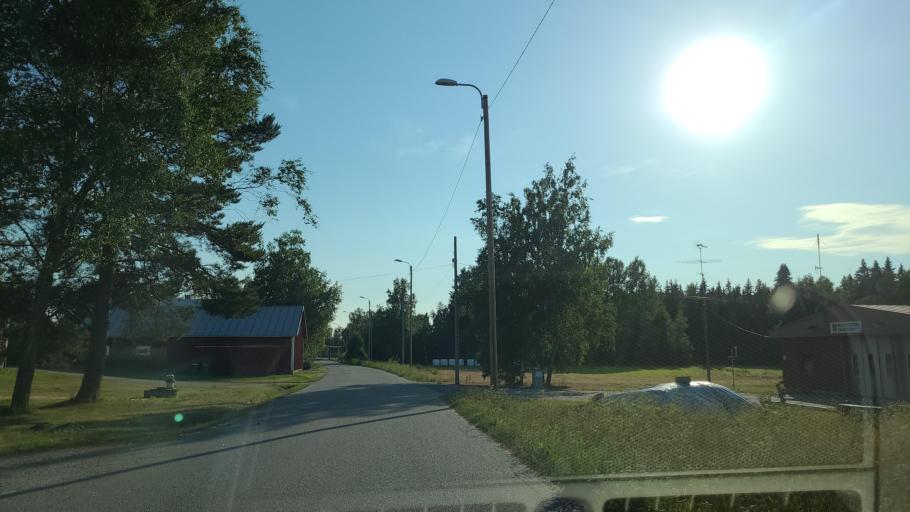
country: FI
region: Ostrobothnia
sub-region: Vaasa
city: Replot
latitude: 63.3466
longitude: 21.3252
